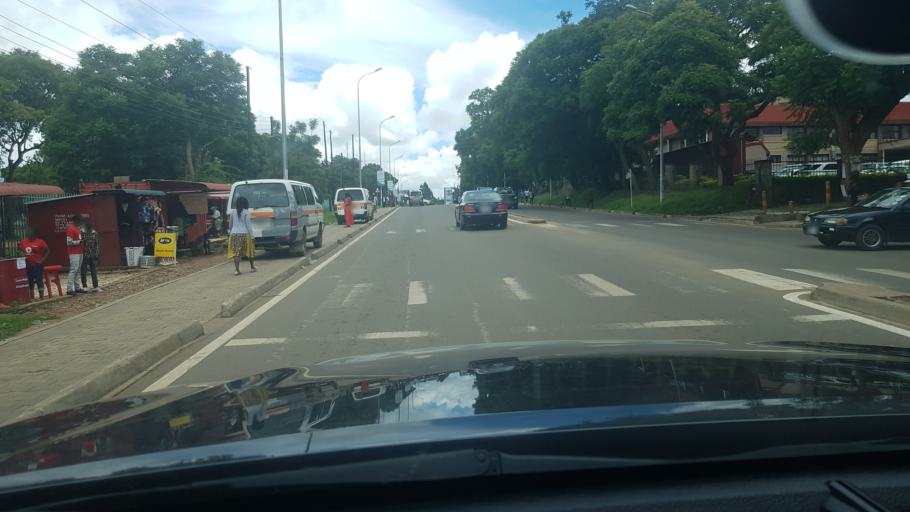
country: ZM
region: Lusaka
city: Lusaka
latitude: -15.4286
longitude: 28.3119
